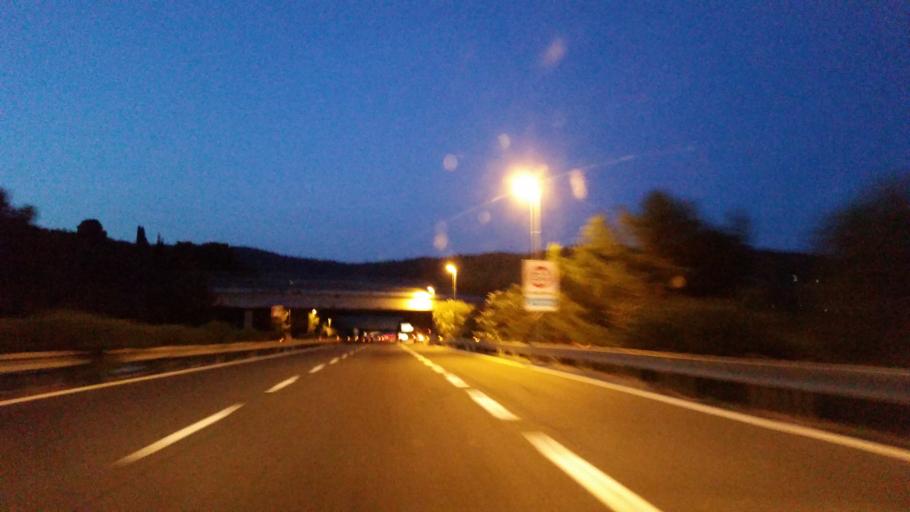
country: IT
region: Liguria
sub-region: Provincia di Imperia
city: San Bartolomeo al Mare
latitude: 43.9266
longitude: 8.0962
